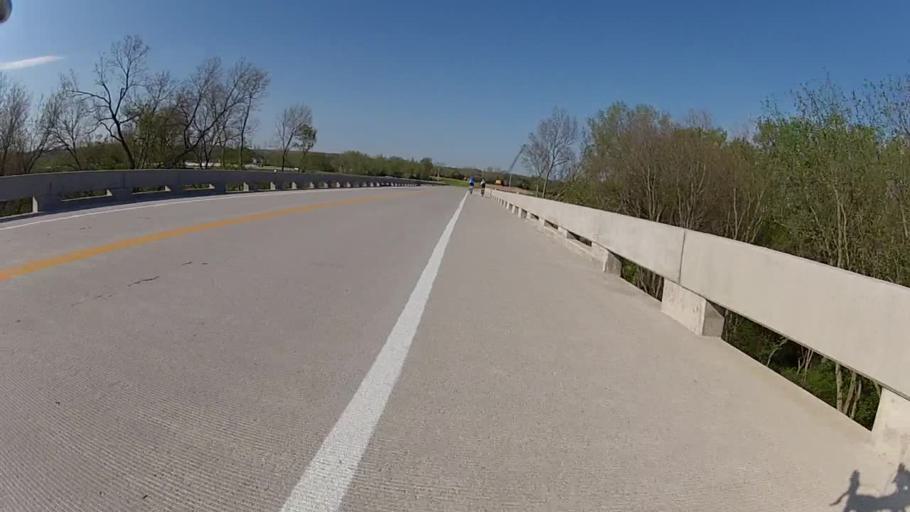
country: US
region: Kansas
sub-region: Riley County
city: Ogden
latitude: 39.1196
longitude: -96.6996
